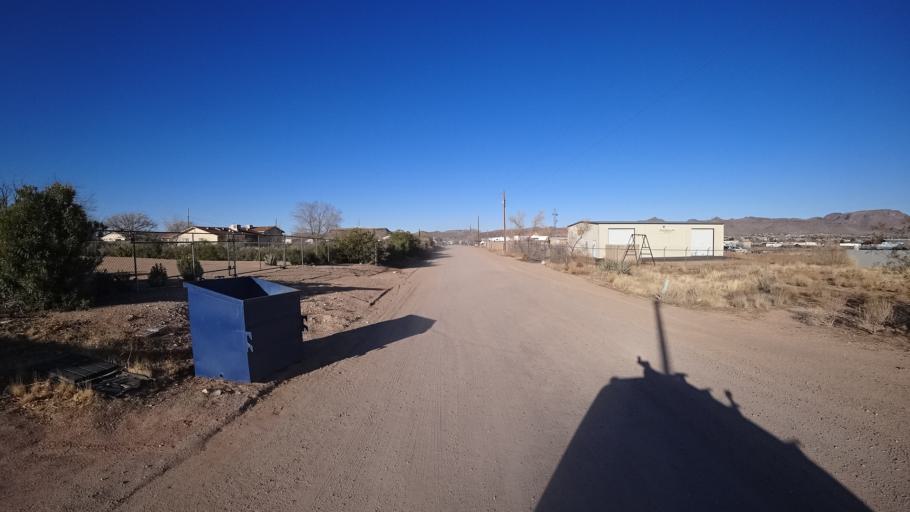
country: US
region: Arizona
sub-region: Mohave County
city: Kingman
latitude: 35.2027
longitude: -114.0164
